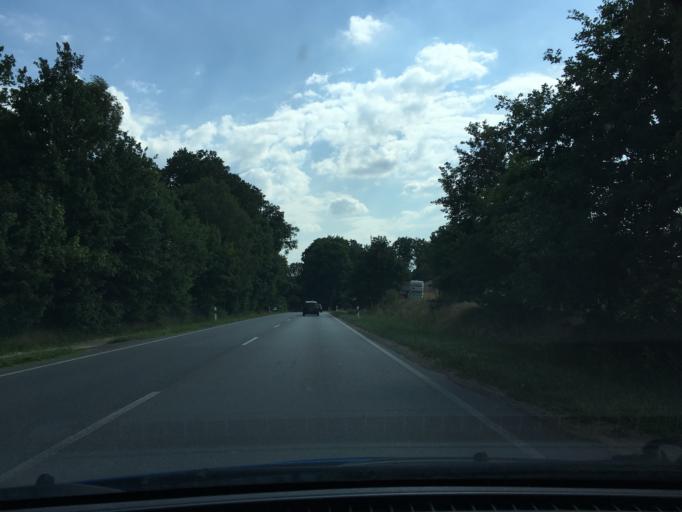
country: DE
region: Lower Saxony
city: Welle
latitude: 53.2465
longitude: 9.8067
